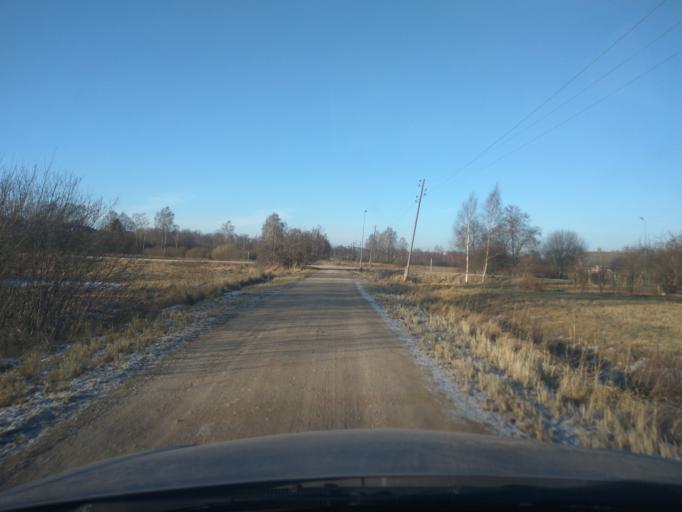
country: LV
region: Kuldigas Rajons
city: Kuldiga
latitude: 56.9606
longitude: 21.9635
